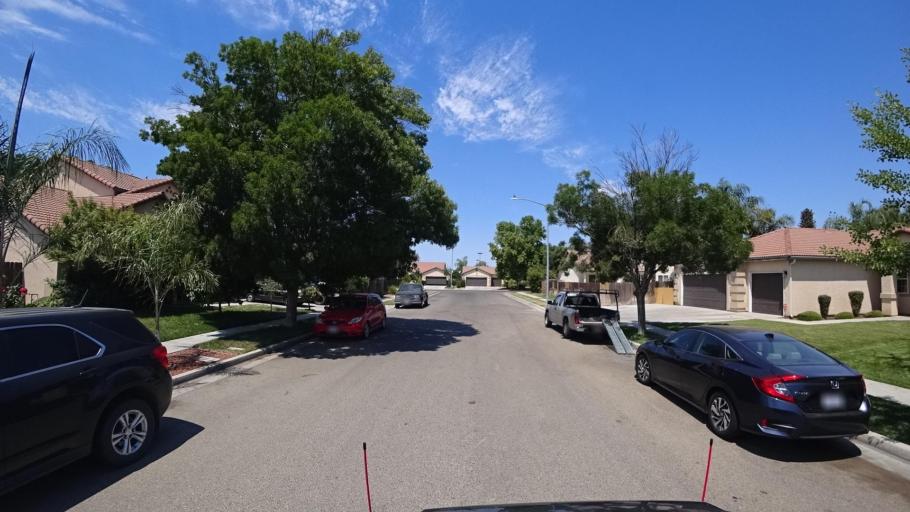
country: US
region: California
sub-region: Fresno County
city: Sunnyside
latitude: 36.7310
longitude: -119.7203
